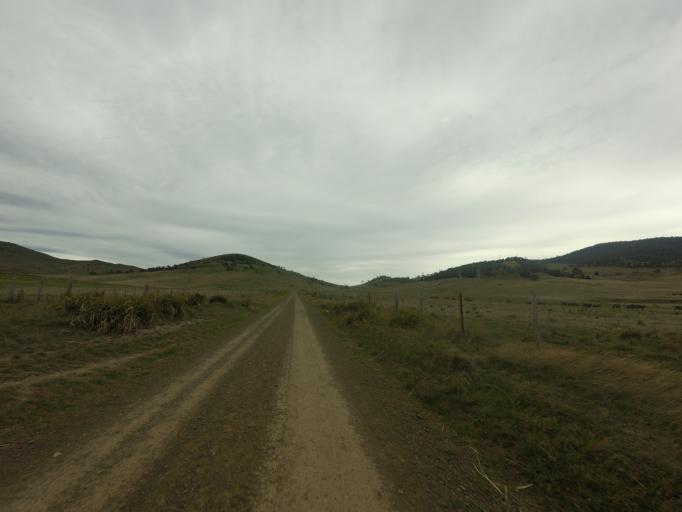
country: AU
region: Tasmania
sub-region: Derwent Valley
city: New Norfolk
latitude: -42.3837
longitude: 146.8713
